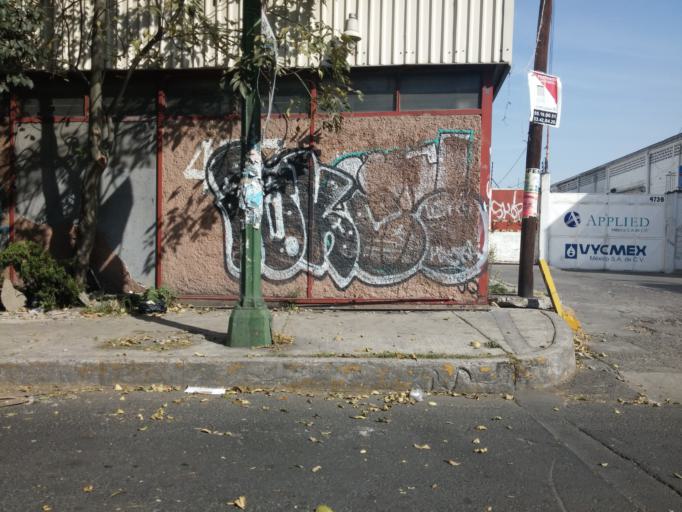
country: MX
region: Mexico City
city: Azcapotzalco
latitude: 19.4836
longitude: -99.1744
